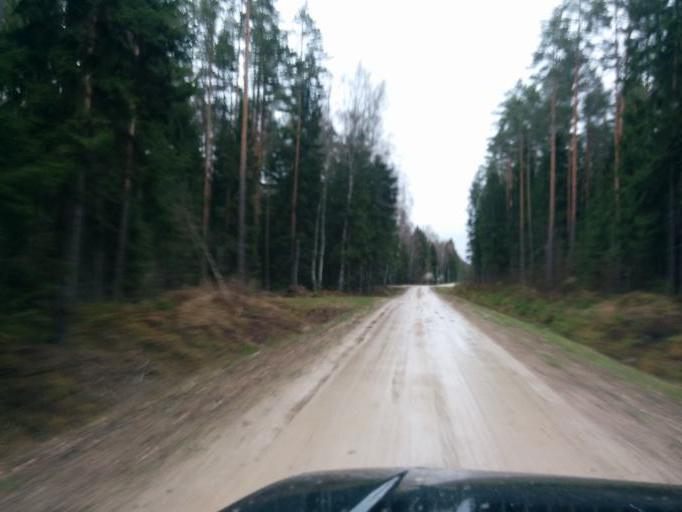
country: LV
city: Tireli
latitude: 56.8161
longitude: 23.6896
